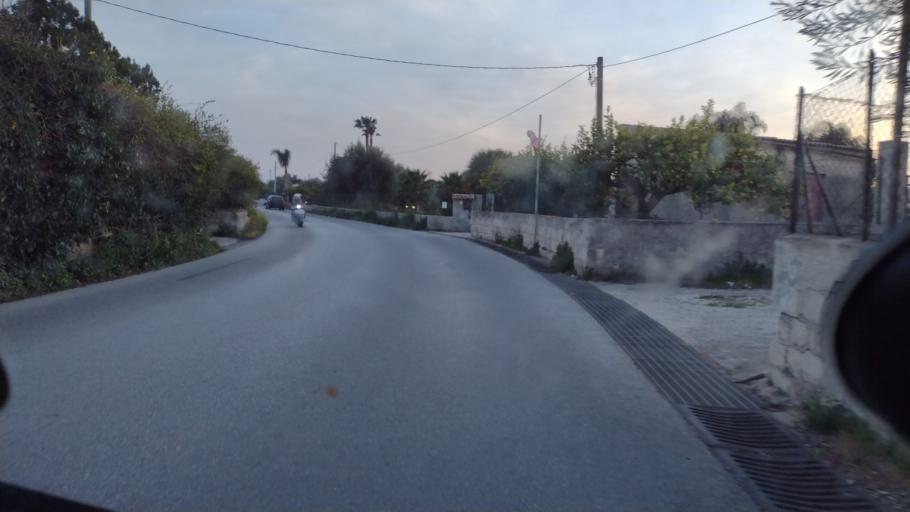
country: IT
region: Sicily
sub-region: Provincia di Siracusa
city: Avola
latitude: 36.8776
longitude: 15.1275
